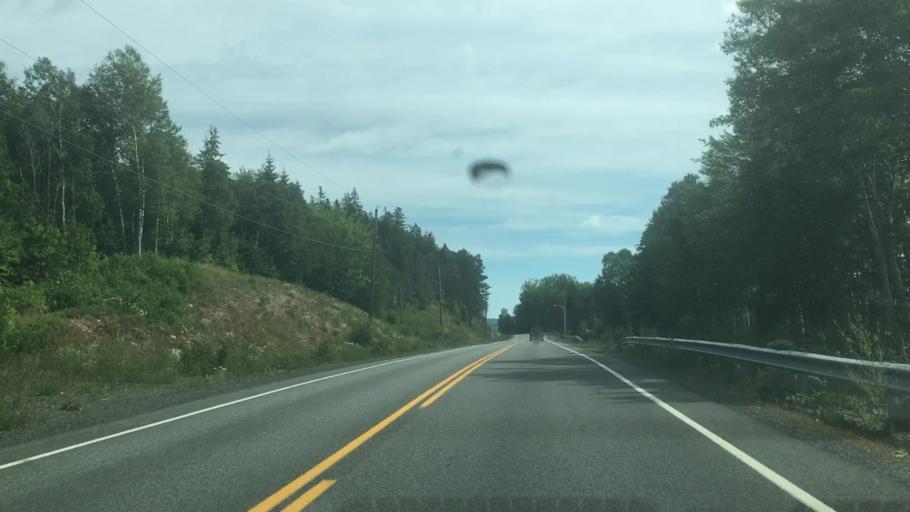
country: CA
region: Nova Scotia
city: Sydney Mines
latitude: 46.2659
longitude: -60.6164
